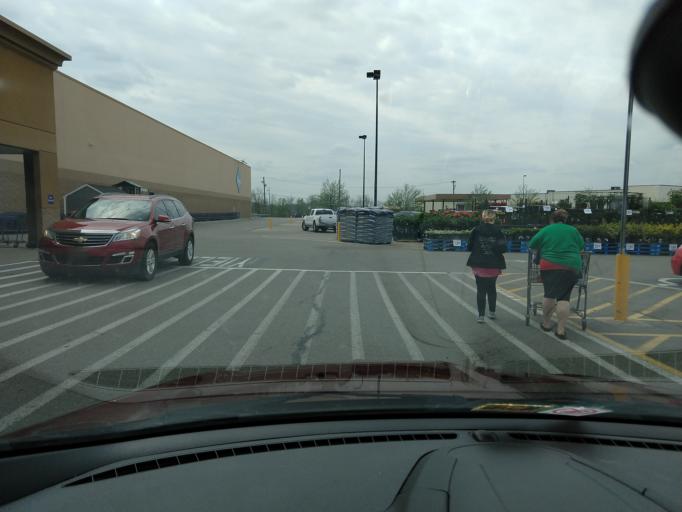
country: US
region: West Virginia
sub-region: Harrison County
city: Bridgeport
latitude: 39.2758
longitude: -80.2799
